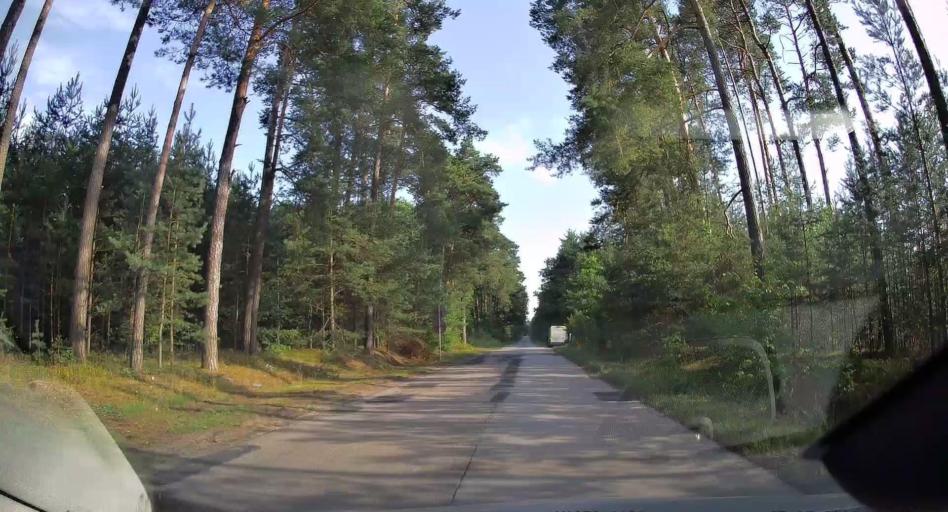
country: PL
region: Swietokrzyskie
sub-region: Powiat konecki
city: Konskie
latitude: 51.2332
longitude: 20.3822
